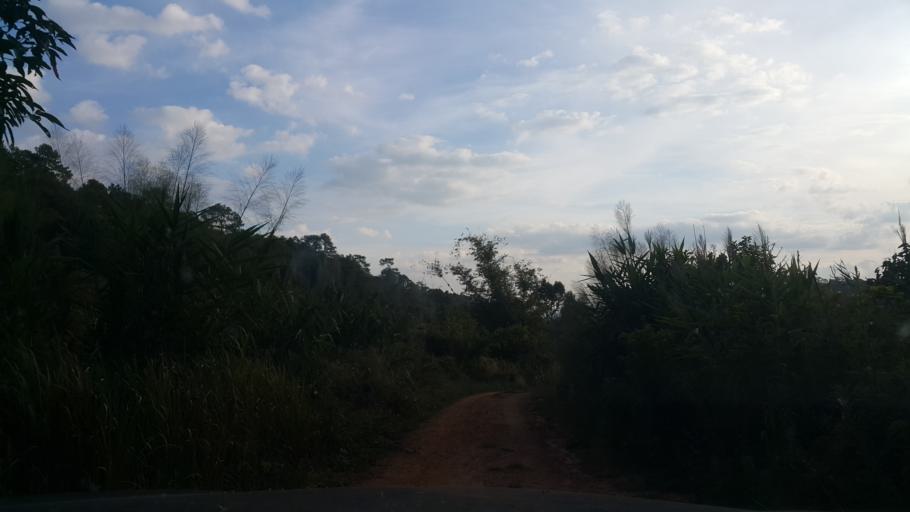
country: TH
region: Chiang Mai
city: Samoeng
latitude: 19.0107
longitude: 98.6489
